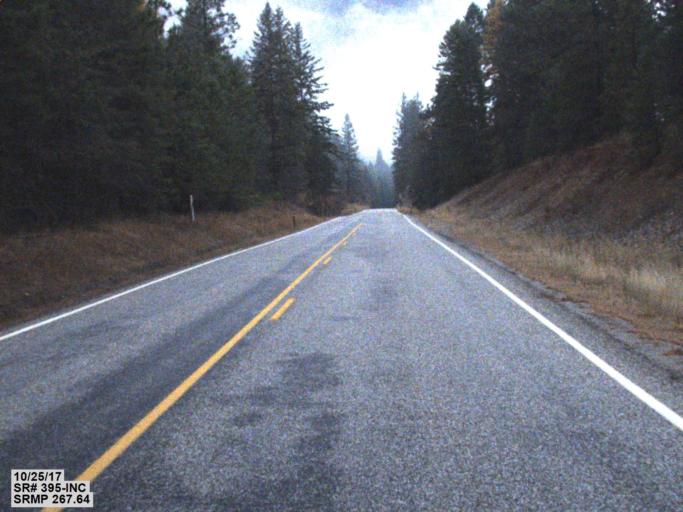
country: CA
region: British Columbia
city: Grand Forks
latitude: 48.9637
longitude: -118.2164
